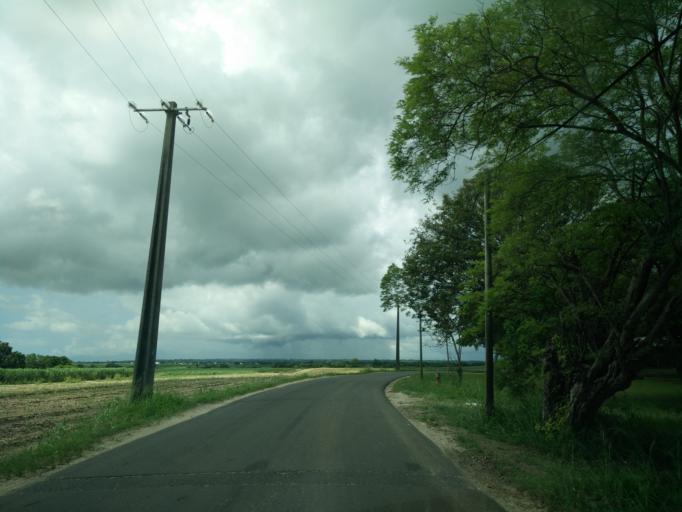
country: GP
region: Guadeloupe
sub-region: Guadeloupe
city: Le Moule
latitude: 16.3020
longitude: -61.3294
